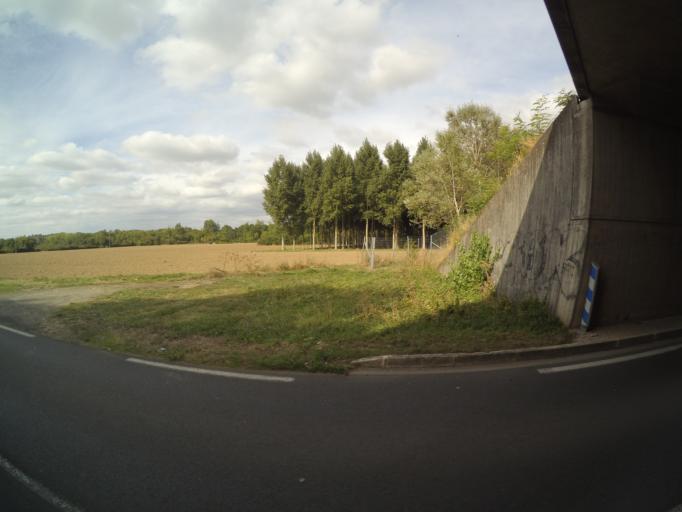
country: FR
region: Centre
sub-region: Departement d'Indre-et-Loire
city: Vouvray
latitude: 47.4048
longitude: 0.8105
